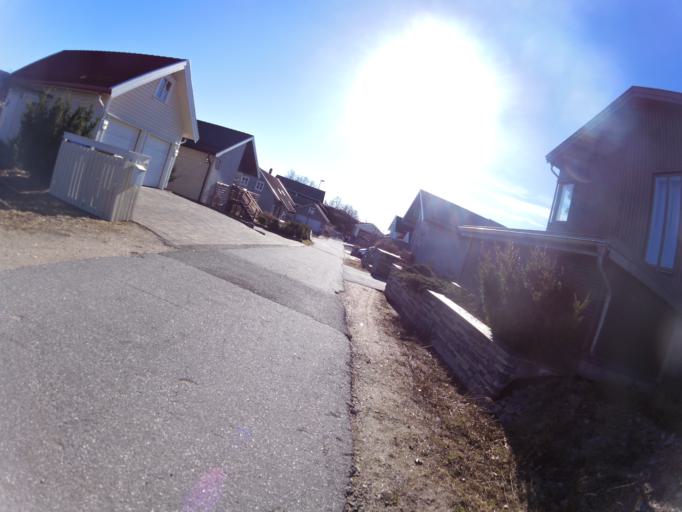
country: NO
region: Ostfold
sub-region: Fredrikstad
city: Fredrikstad
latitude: 59.2135
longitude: 10.9051
